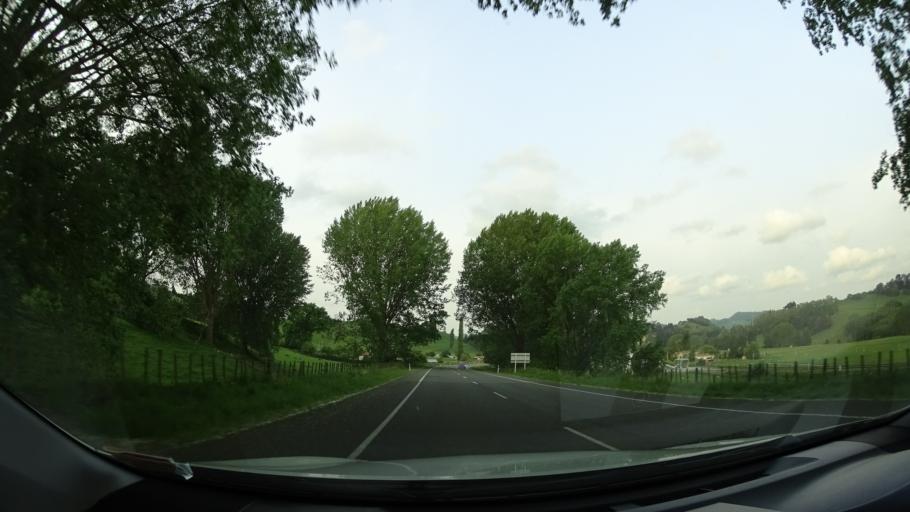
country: NZ
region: Manawatu-Wanganui
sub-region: Ruapehu District
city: Waiouru
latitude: -39.7386
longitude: 175.8402
